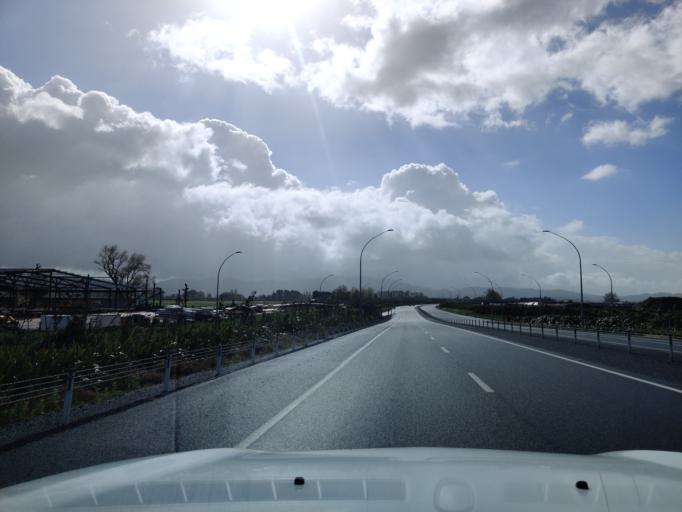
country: NZ
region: Waikato
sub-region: Waipa District
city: Cambridge
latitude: -37.8685
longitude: 175.4616
